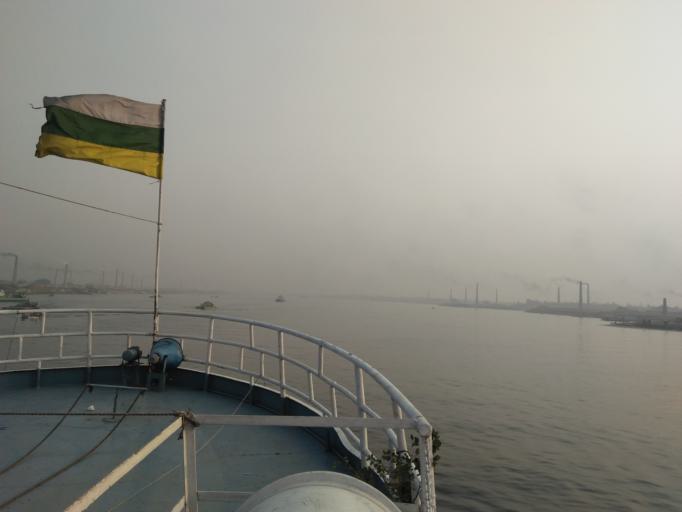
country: BD
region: Dhaka
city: Narayanganj
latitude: 23.6229
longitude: 90.4534
